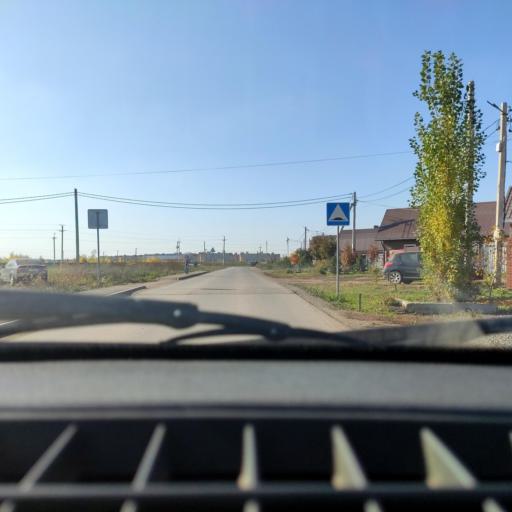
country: RU
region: Bashkortostan
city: Ufa
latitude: 54.6233
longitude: 55.9010
